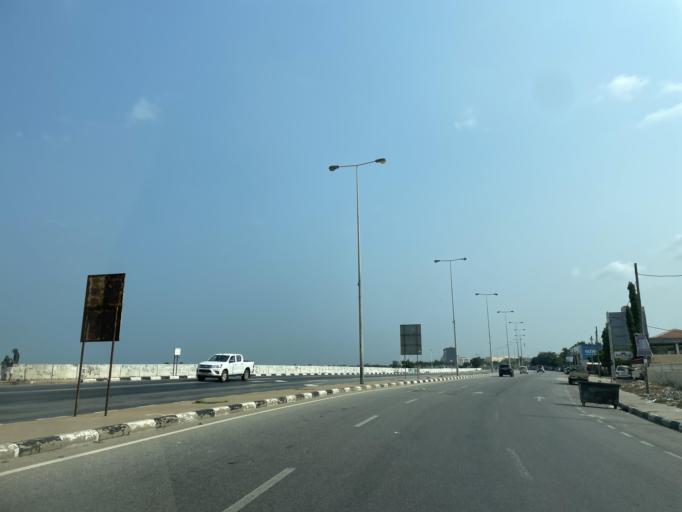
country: AO
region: Luanda
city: Luanda
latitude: -8.8279
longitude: 13.2142
